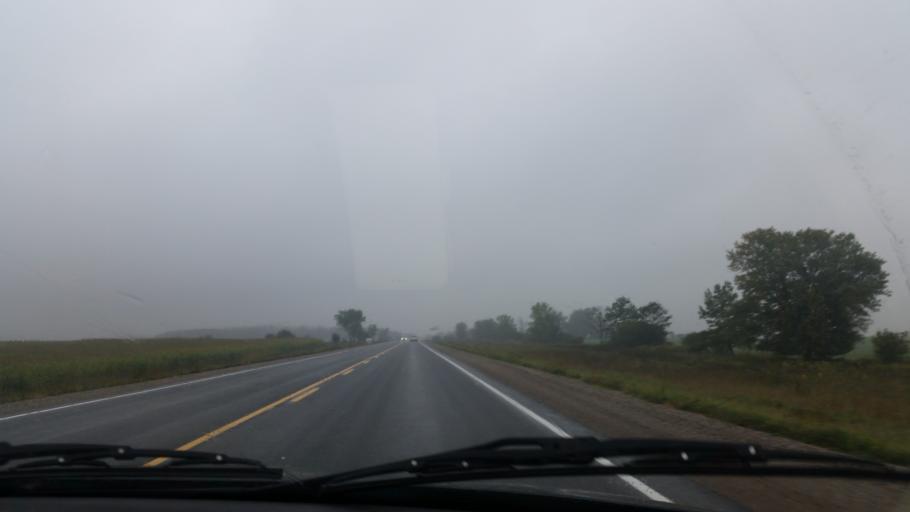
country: CA
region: Ontario
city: Stratford
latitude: 43.2556
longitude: -81.0789
